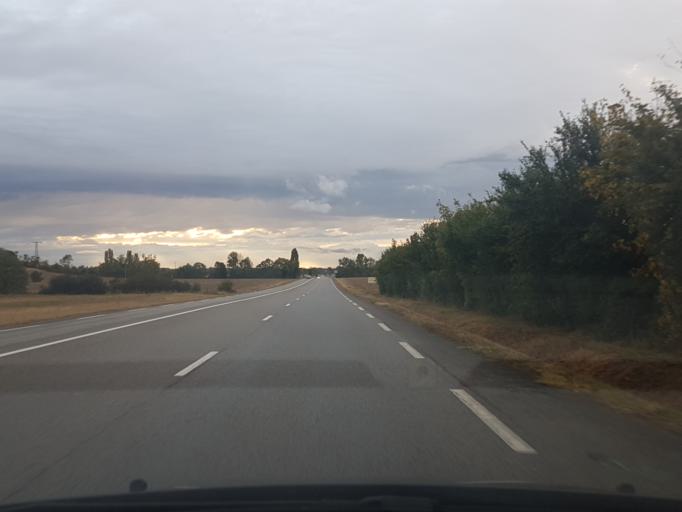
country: FR
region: Midi-Pyrenees
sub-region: Departement de l'Ariege
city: Mirepoix
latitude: 43.0750
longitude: 1.7823
